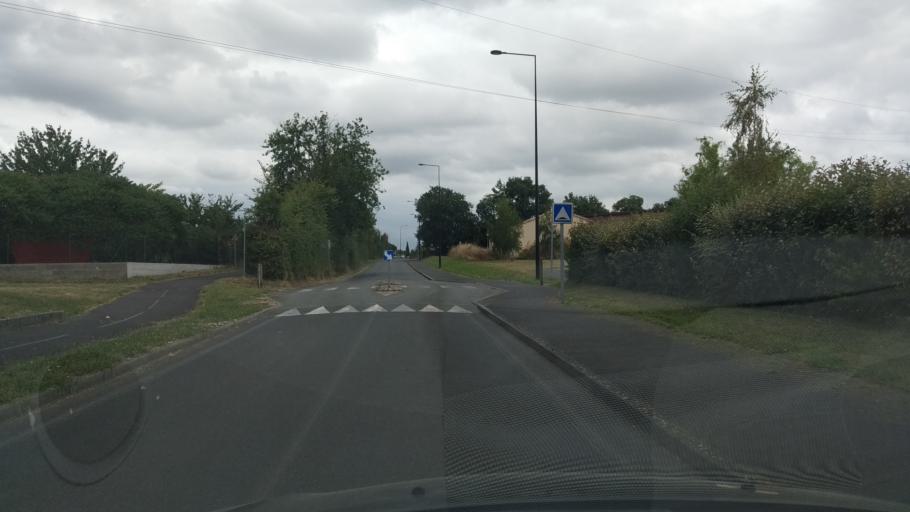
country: FR
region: Poitou-Charentes
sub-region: Departement de la Vienne
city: Smarves
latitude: 46.5096
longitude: 0.3549
